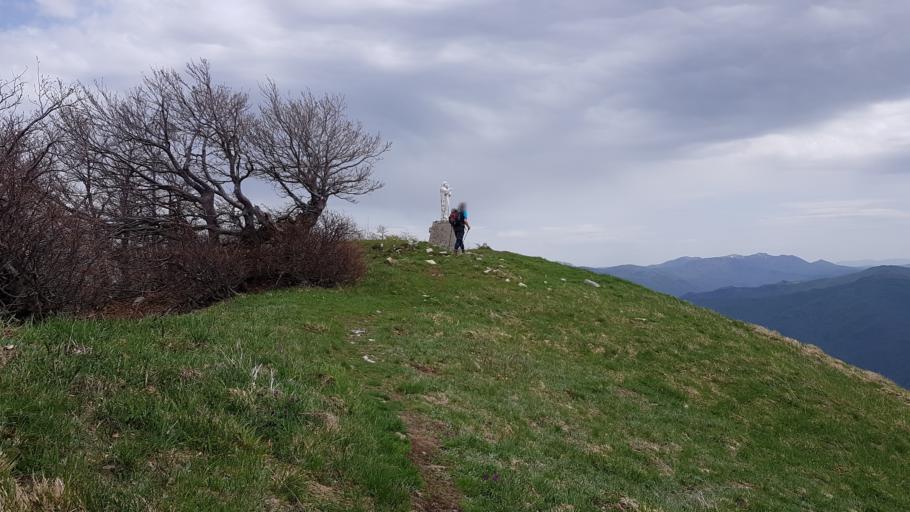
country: IT
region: Liguria
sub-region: Provincia di Genova
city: Gorreto
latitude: 44.6314
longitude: 9.2744
